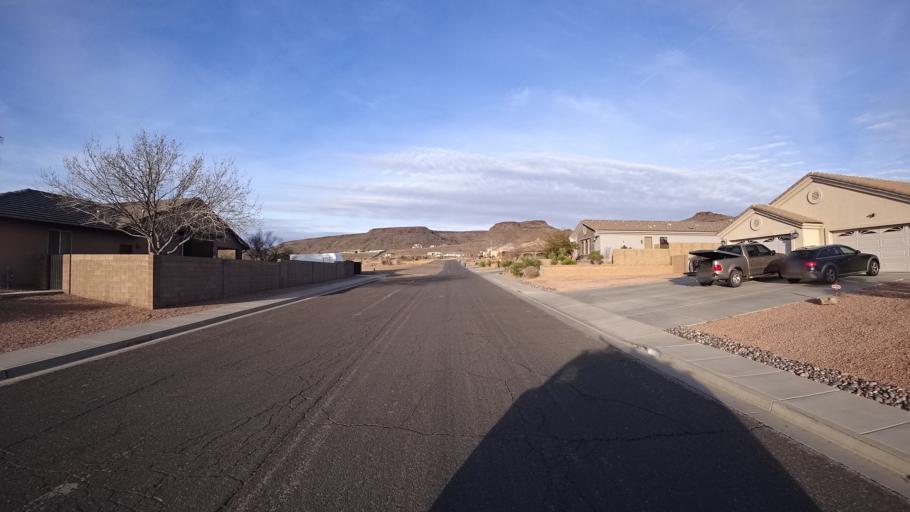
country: US
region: Arizona
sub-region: Mohave County
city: New Kingman-Butler
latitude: 35.2419
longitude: -114.0465
